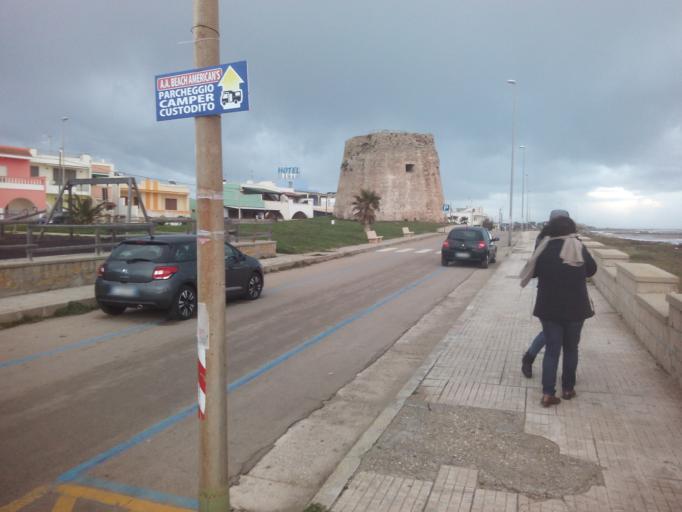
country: IT
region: Apulia
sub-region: Provincia di Lecce
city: Gemini
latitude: 39.8588
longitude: 18.1640
